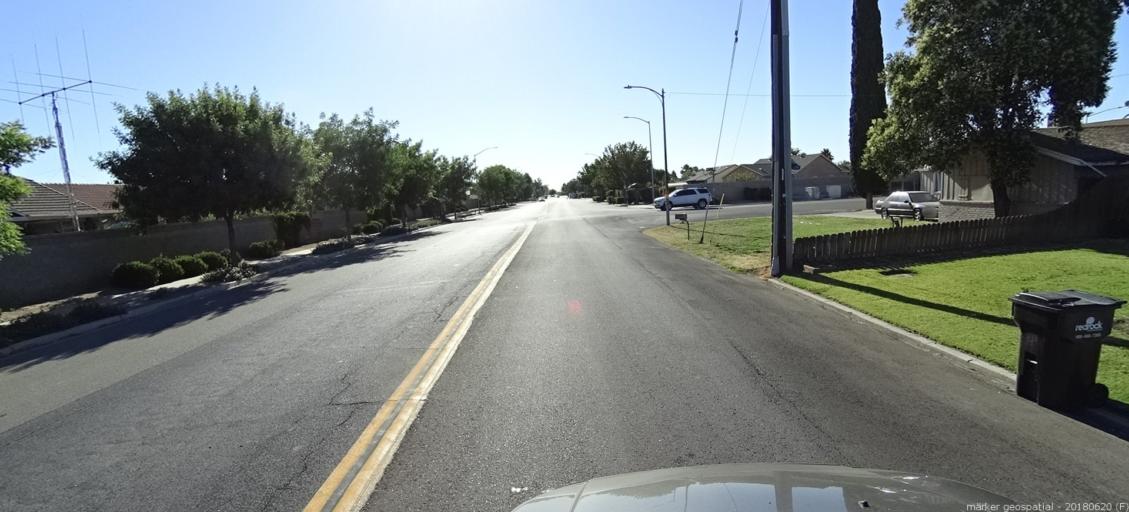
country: US
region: California
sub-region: Madera County
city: Parkwood
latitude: 36.9382
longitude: -120.0487
